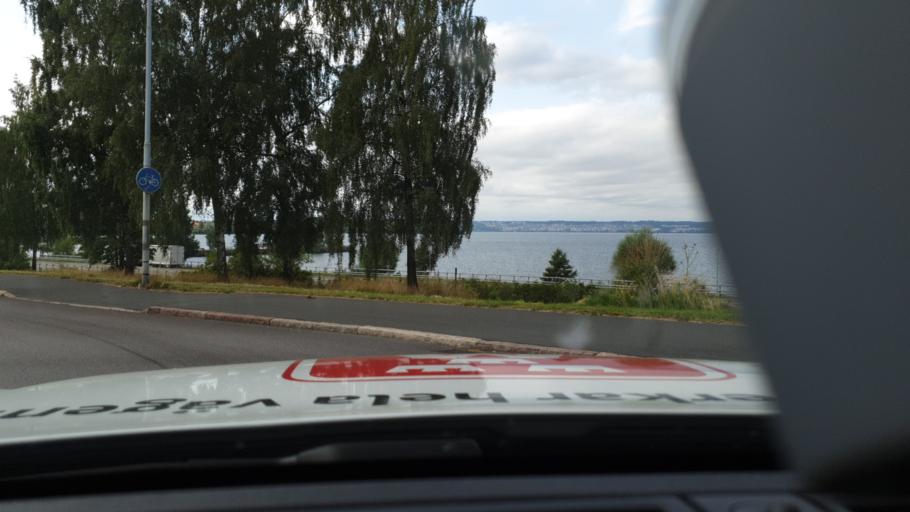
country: SE
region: Joenkoeping
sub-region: Jonkopings Kommun
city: Huskvarna
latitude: 57.7990
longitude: 14.2714
